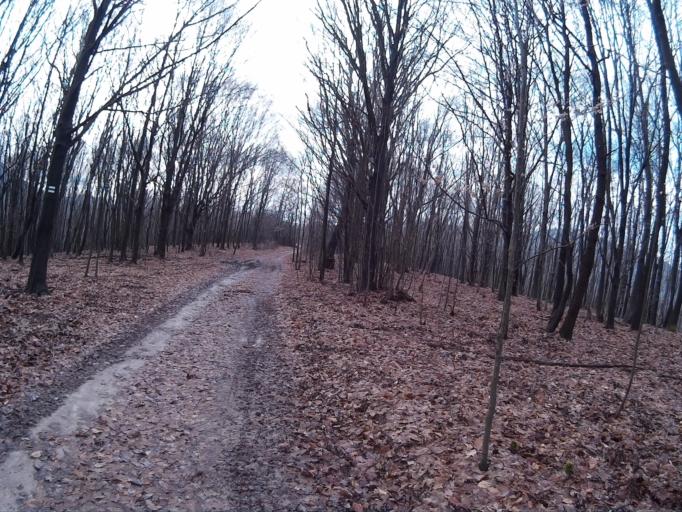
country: HU
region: Borsod-Abauj-Zemplen
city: Satoraljaujhely
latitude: 48.4101
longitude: 21.5988
